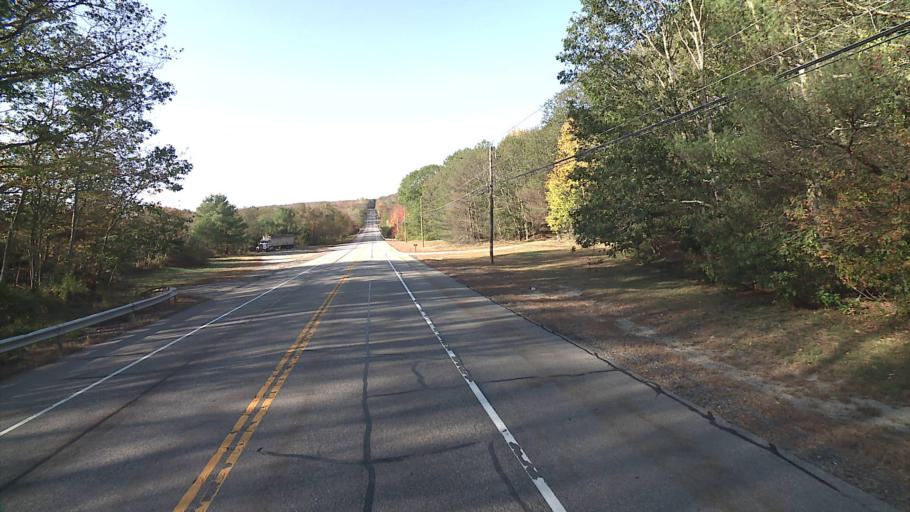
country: US
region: Connecticut
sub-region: Windham County
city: Wauregan
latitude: 41.7737
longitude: -72.0407
